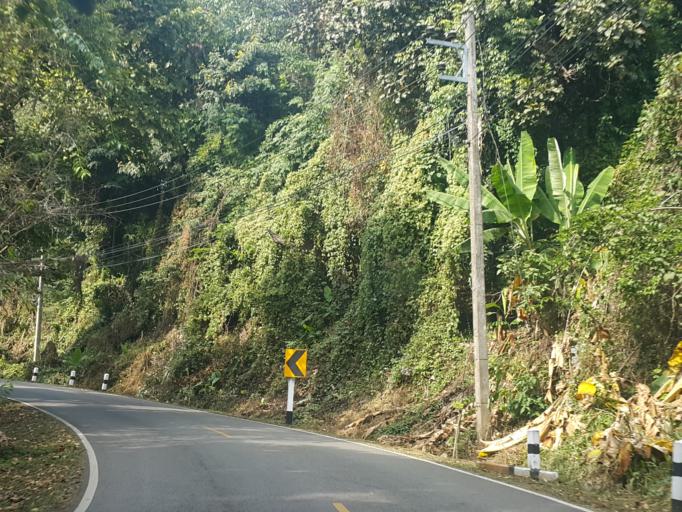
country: TH
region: Chiang Mai
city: Samoeng
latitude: 18.9196
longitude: 98.8209
